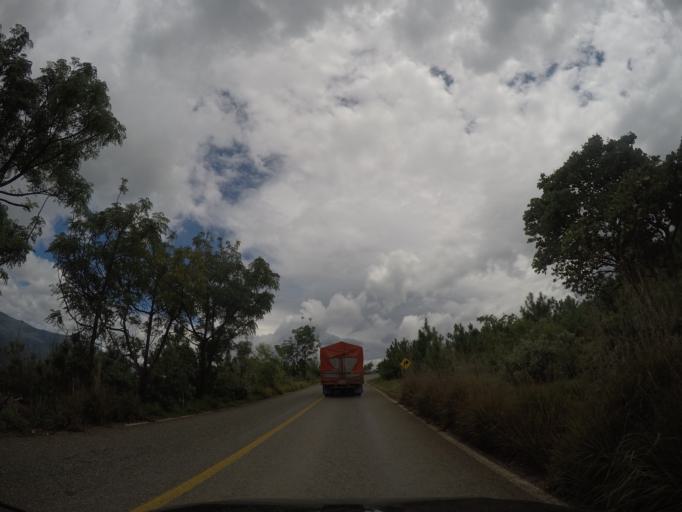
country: MX
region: Oaxaca
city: San Francisco Sola
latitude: 16.4836
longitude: -96.9803
